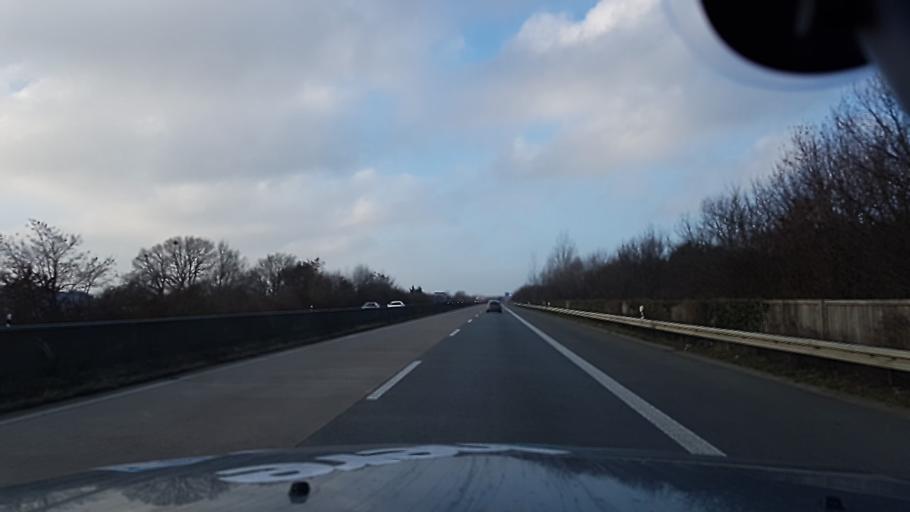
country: DE
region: North Rhine-Westphalia
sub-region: Regierungsbezirk Munster
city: Dreierwalde
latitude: 52.2964
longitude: 7.5108
